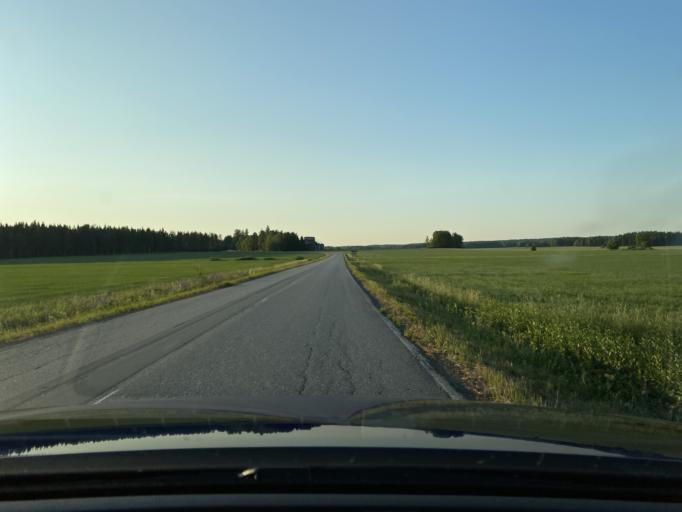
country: FI
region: Haeme
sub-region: Forssa
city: Humppila
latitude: 61.0101
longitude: 23.2536
